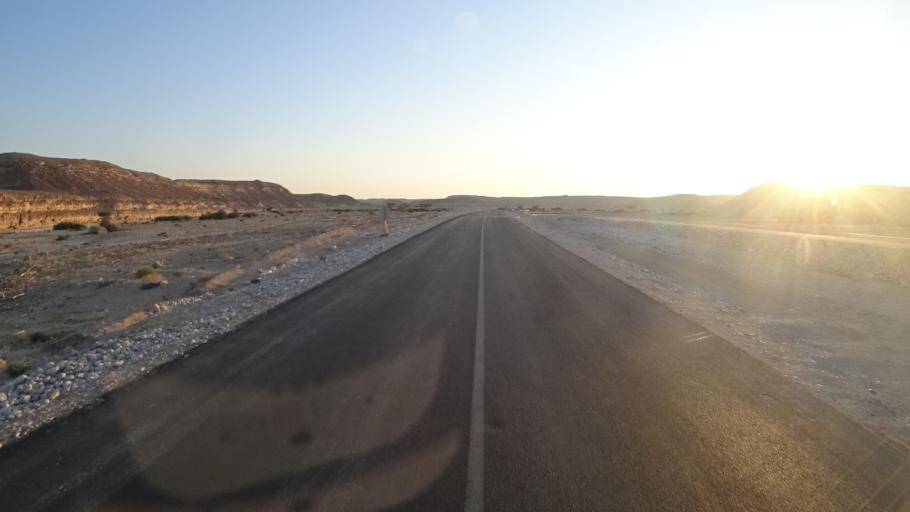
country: OM
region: Zufar
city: Salalah
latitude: 17.5153
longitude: 53.3736
